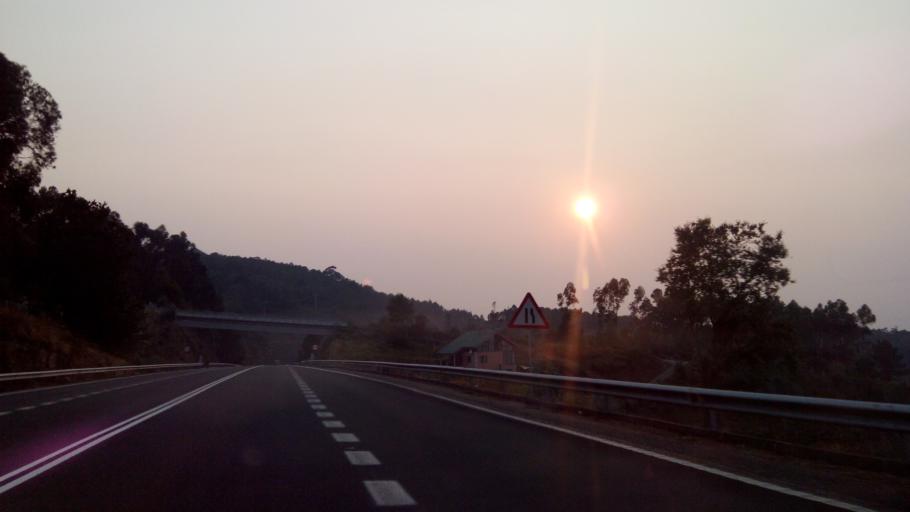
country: ES
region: Galicia
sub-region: Provincia de Pontevedra
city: Baiona
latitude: 42.1131
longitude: -8.8524
